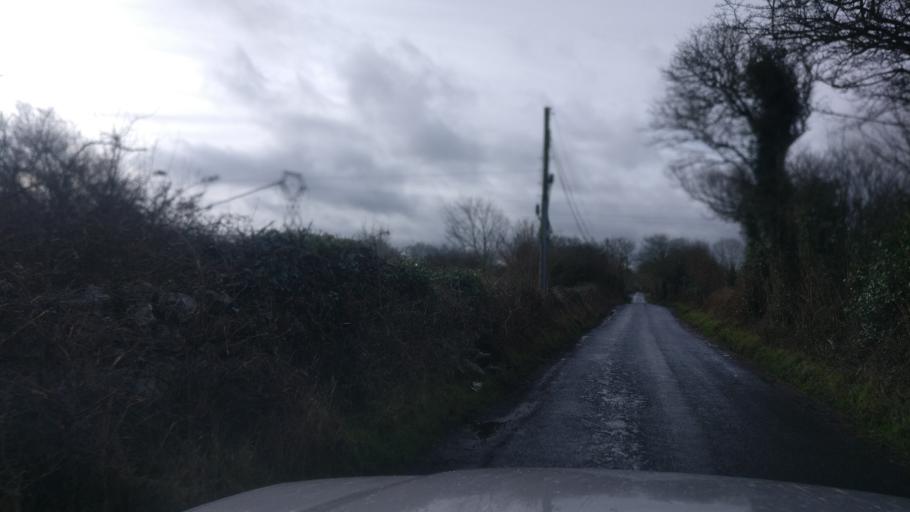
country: IE
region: Connaught
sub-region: County Galway
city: Athenry
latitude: 53.2765
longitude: -8.7664
